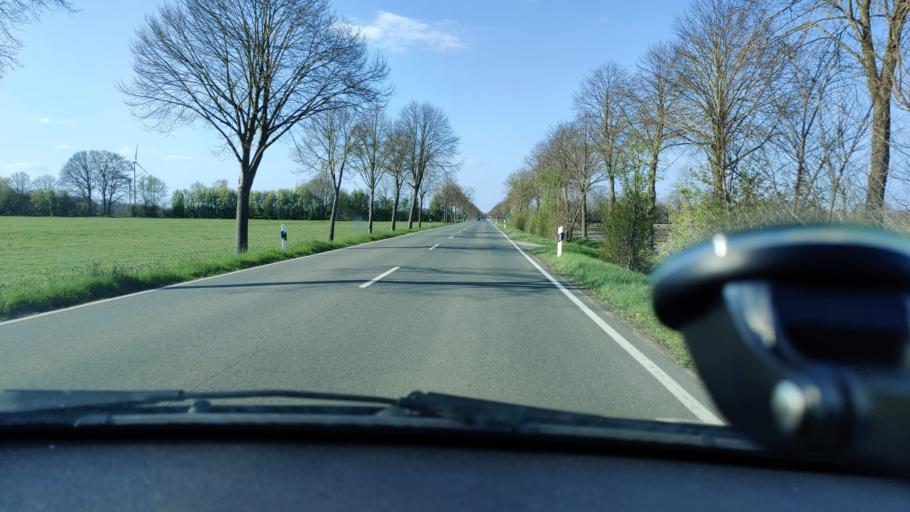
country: DE
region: North Rhine-Westphalia
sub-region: Regierungsbezirk Munster
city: Gescher
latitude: 51.9123
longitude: 7.0403
